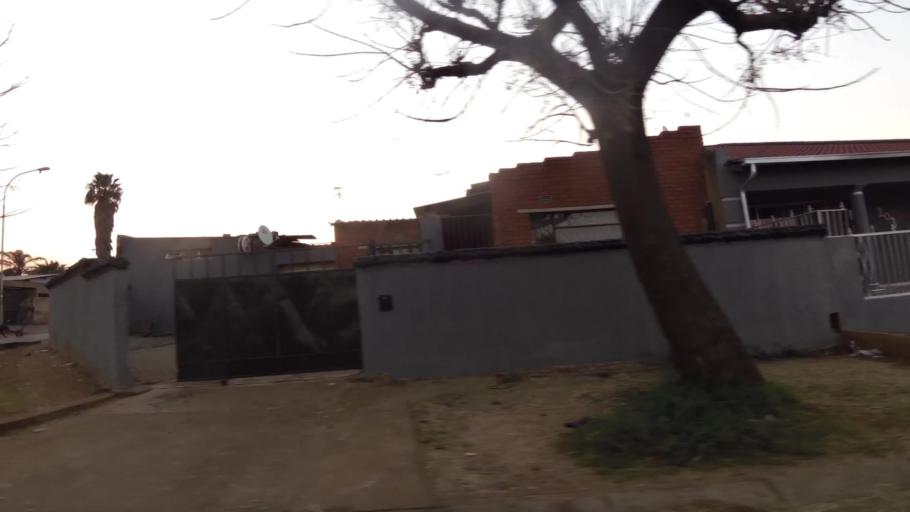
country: ZA
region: Gauteng
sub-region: City of Johannesburg Metropolitan Municipality
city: Soweto
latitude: -26.2848
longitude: 27.8784
